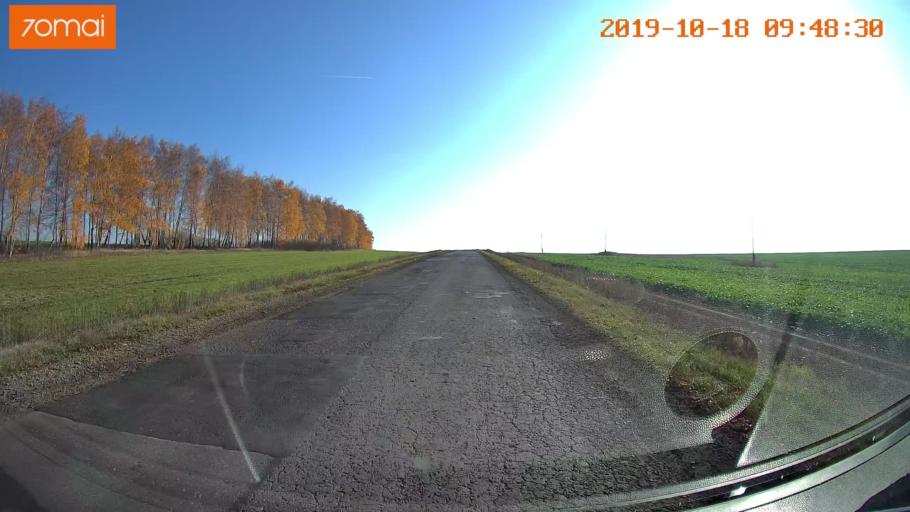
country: RU
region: Tula
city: Kazachka
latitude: 53.3176
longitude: 38.2509
